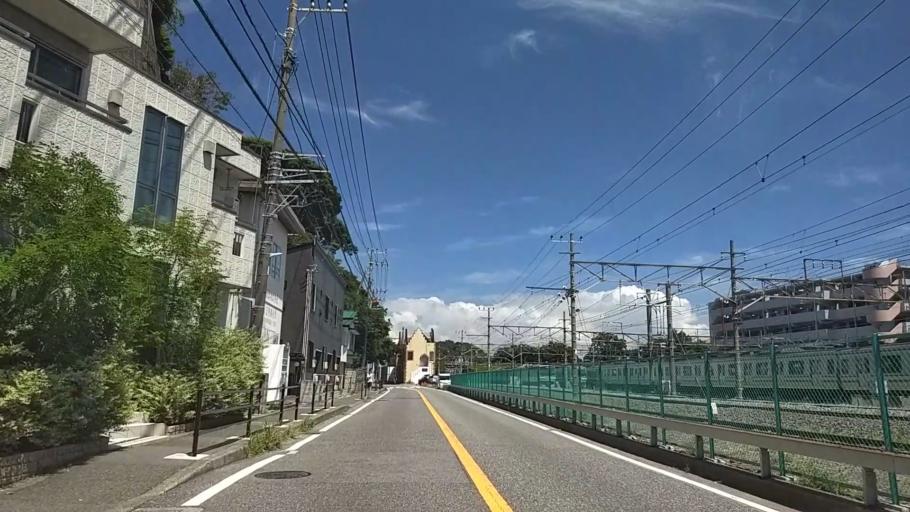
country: JP
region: Kanagawa
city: Zushi
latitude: 35.2986
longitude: 139.5844
